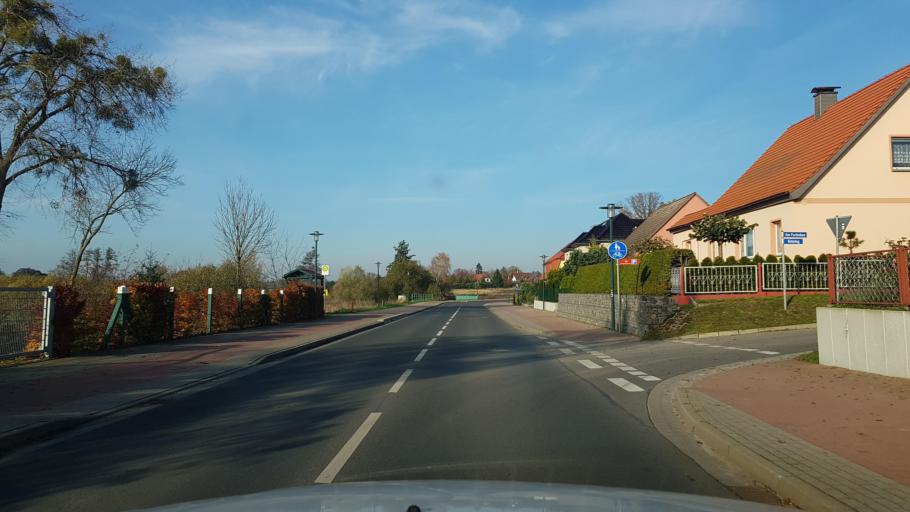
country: DE
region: Brandenburg
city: Brussow
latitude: 53.4640
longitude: 14.2044
